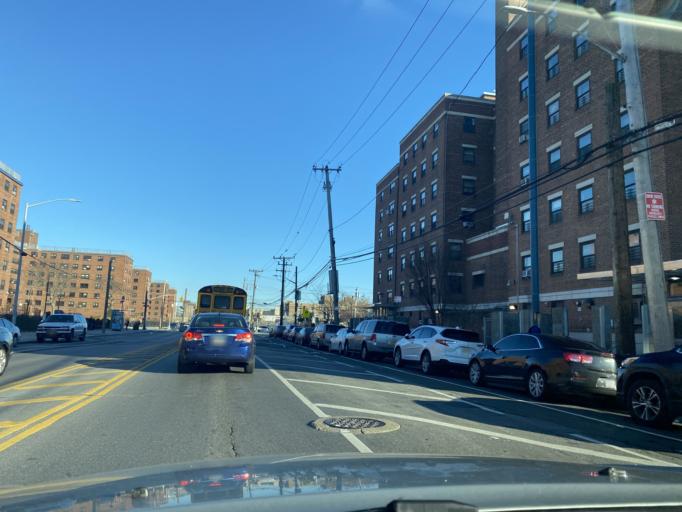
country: US
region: New York
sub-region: Nassau County
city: Inwood
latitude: 40.5950
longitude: -73.7858
